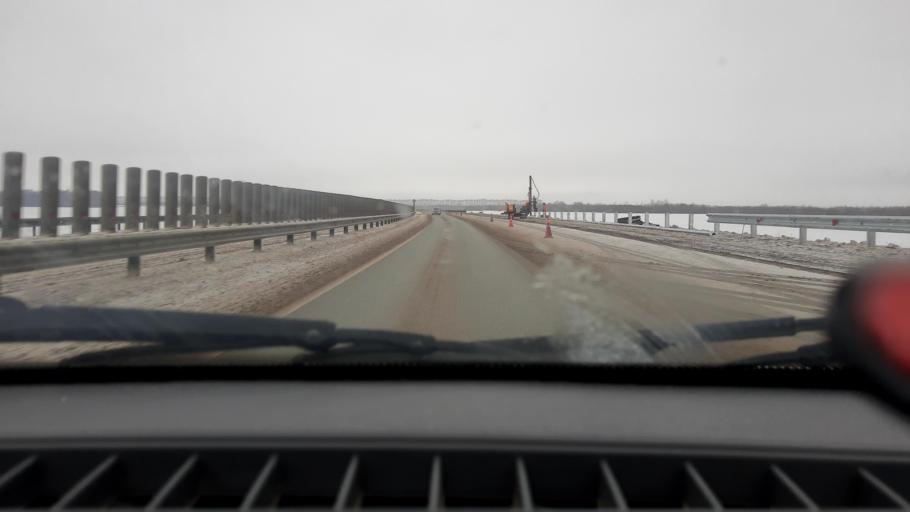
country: RU
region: Bashkortostan
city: Asanovo
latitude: 54.9762
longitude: 55.5708
